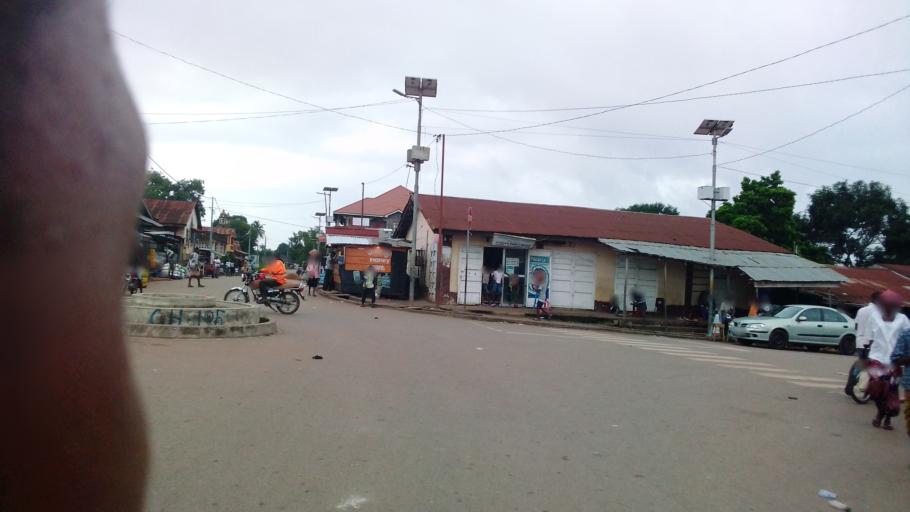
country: SL
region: Northern Province
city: Lunsar
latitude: 8.6840
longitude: -12.5334
